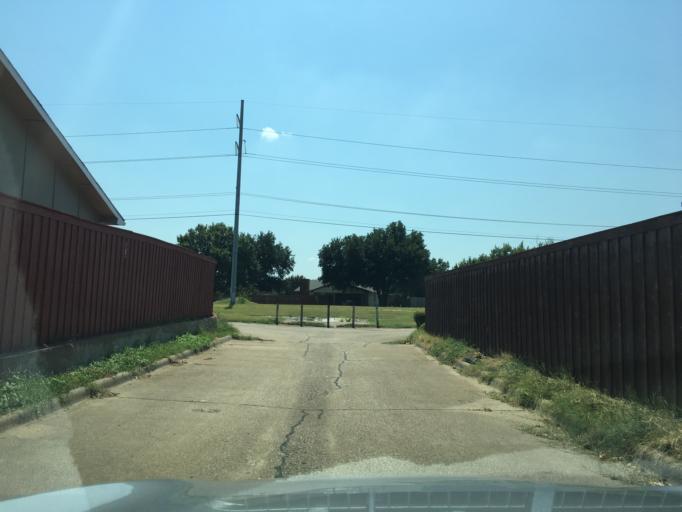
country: US
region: Texas
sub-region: Dallas County
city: Garland
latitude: 32.9553
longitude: -96.6689
